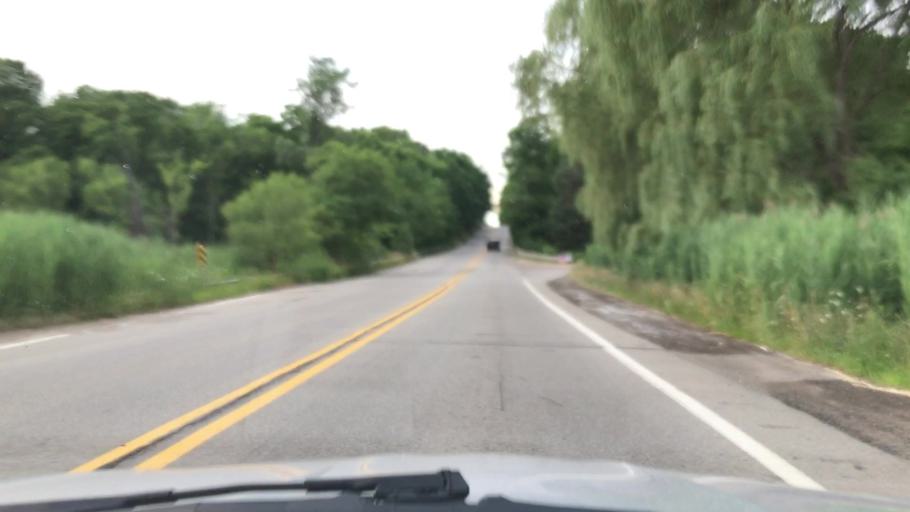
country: US
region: Michigan
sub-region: Wayne County
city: Northville
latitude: 42.4299
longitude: -83.5121
